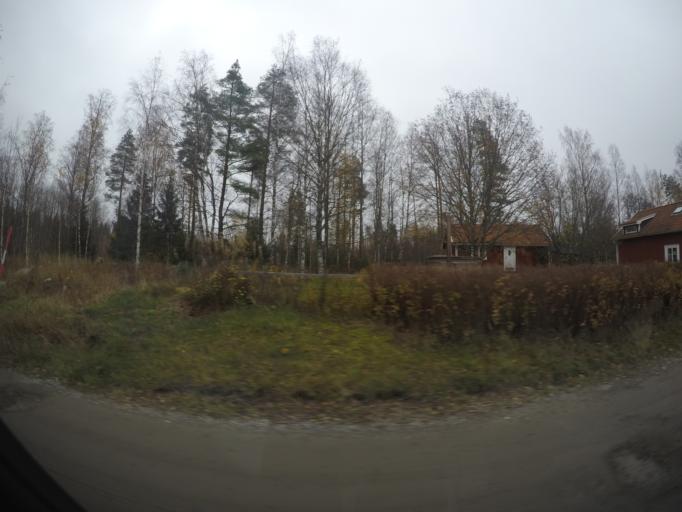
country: SE
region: Vaestmanland
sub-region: Surahammars Kommun
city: Ramnas
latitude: 59.7063
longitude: 16.0916
